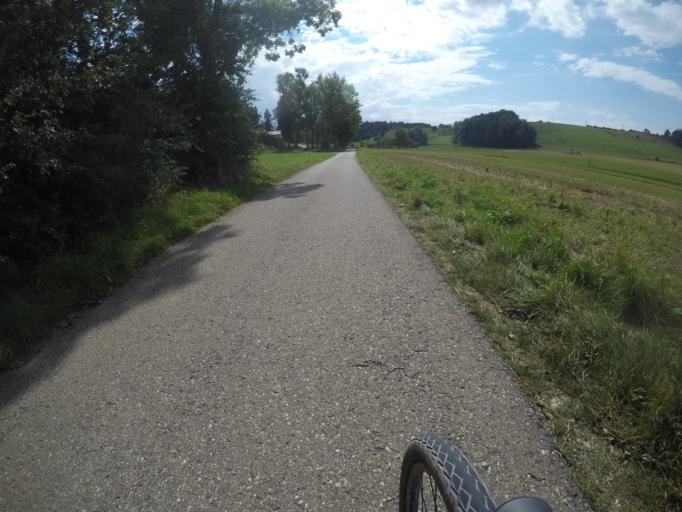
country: DE
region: Baden-Wuerttemberg
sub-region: Tuebingen Region
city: Munsingen
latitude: 48.4032
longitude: 9.4944
